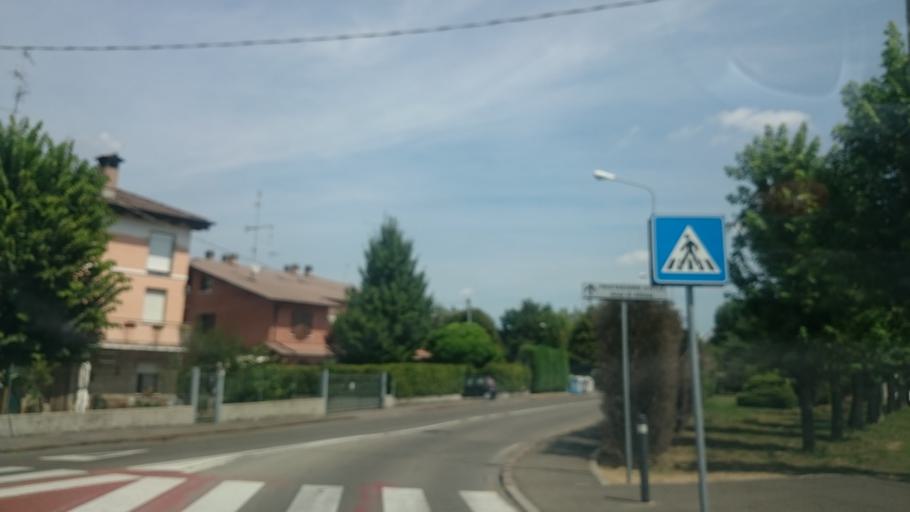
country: IT
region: Emilia-Romagna
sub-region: Provincia di Reggio Emilia
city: Rubiera
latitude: 44.6495
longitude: 10.7736
